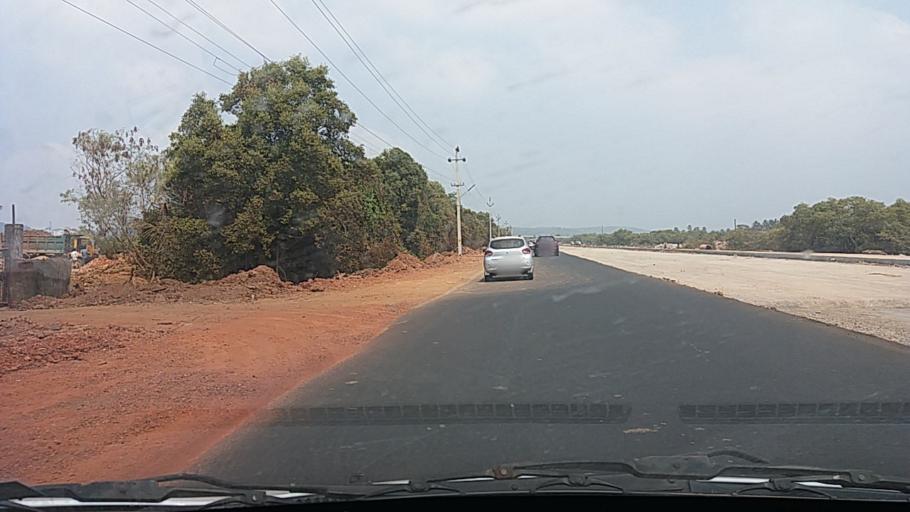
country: IN
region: Goa
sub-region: North Goa
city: Taleigao
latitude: 15.4824
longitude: 73.8473
